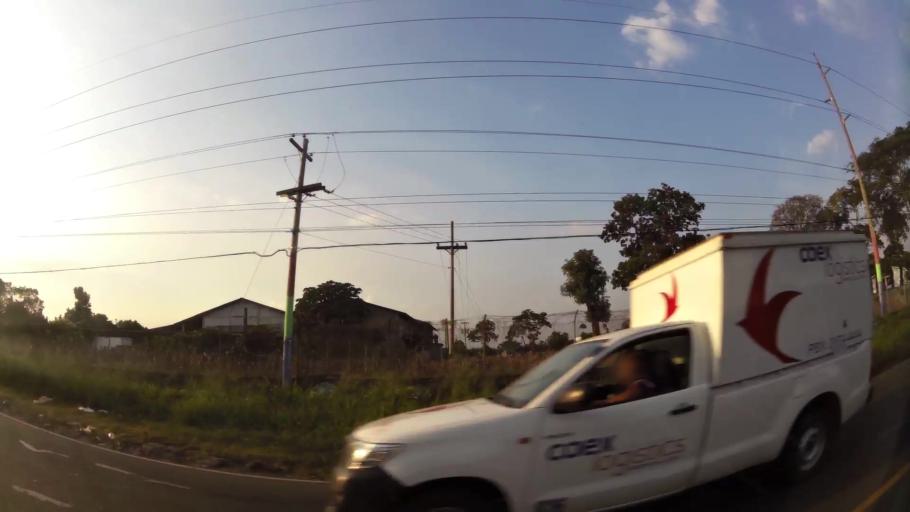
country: GT
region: Retalhuleu
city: San Sebastian
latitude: 14.5499
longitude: -91.6600
